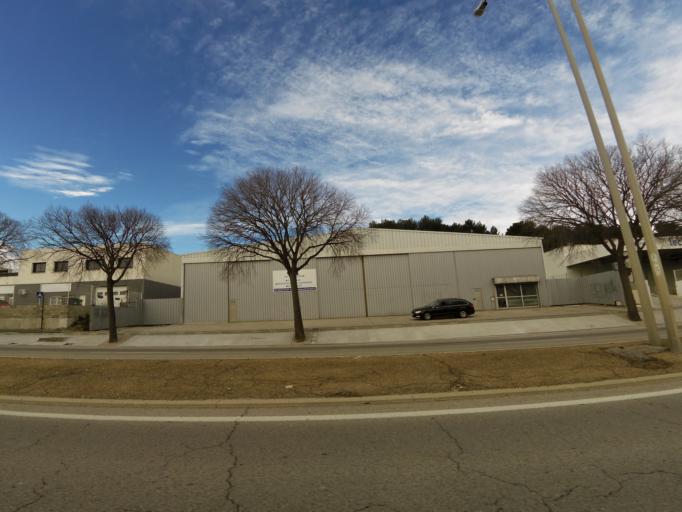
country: FR
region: Languedoc-Roussillon
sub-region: Departement du Gard
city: Milhaud
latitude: 43.8173
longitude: 4.3170
